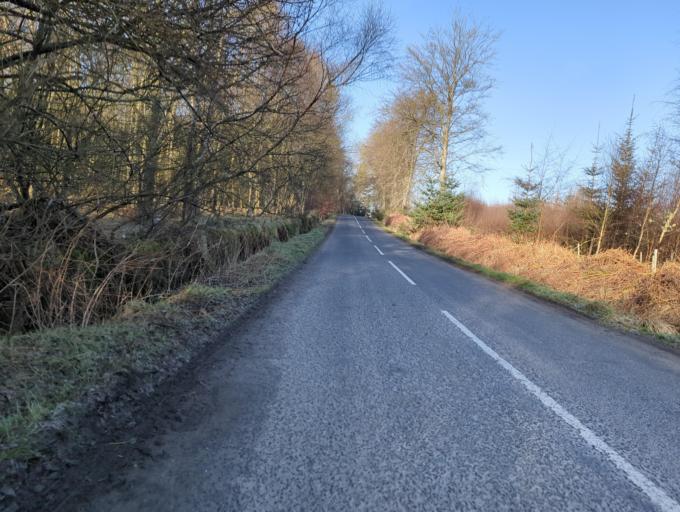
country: GB
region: Scotland
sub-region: Perth and Kinross
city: Methven
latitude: 56.4556
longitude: -3.5801
